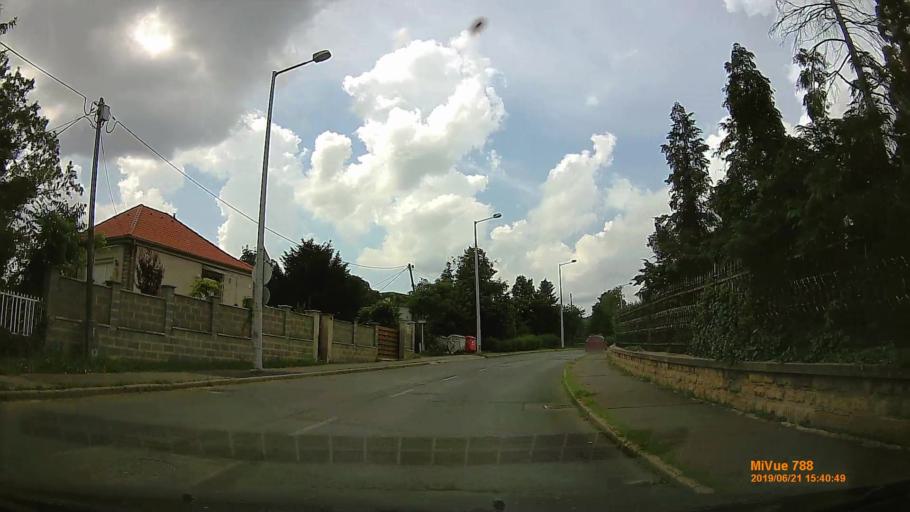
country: HU
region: Baranya
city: Pecs
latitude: 46.0828
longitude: 18.2099
